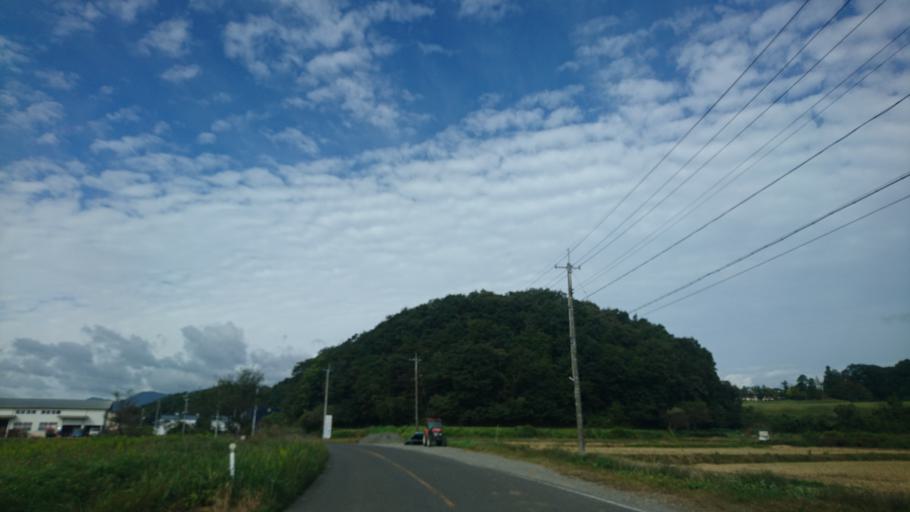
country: JP
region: Fukushima
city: Sukagawa
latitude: 37.3289
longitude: 140.2822
